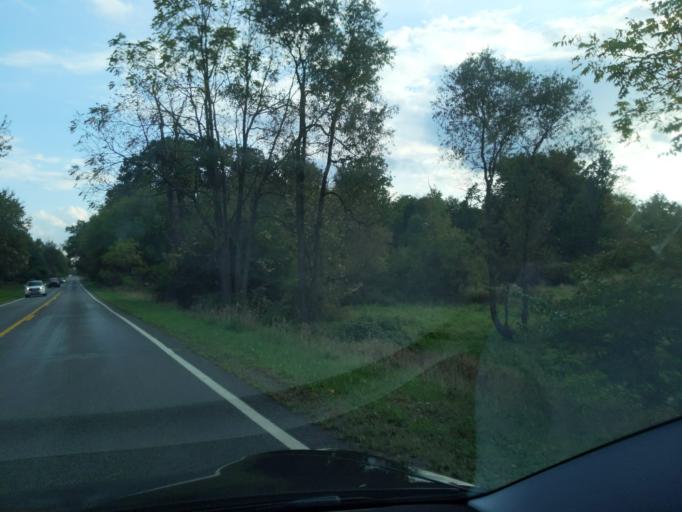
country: US
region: Michigan
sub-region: Jackson County
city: Jackson
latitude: 42.3072
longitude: -84.4628
